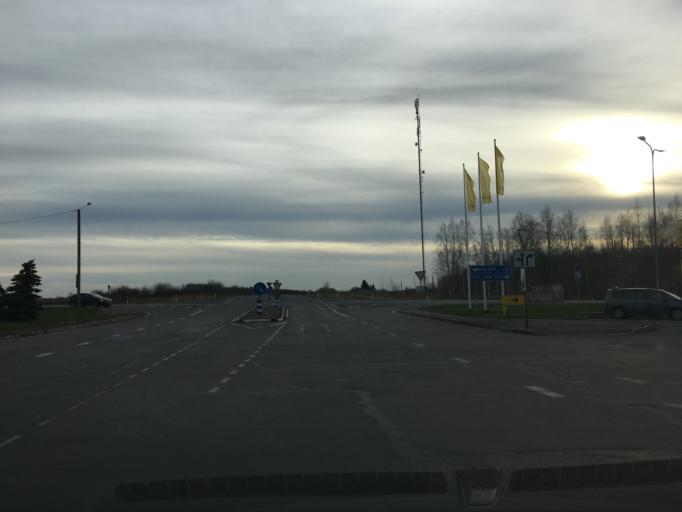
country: EE
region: Ida-Virumaa
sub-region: Sillamaee linn
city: Sillamae
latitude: 59.3913
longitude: 27.7744
